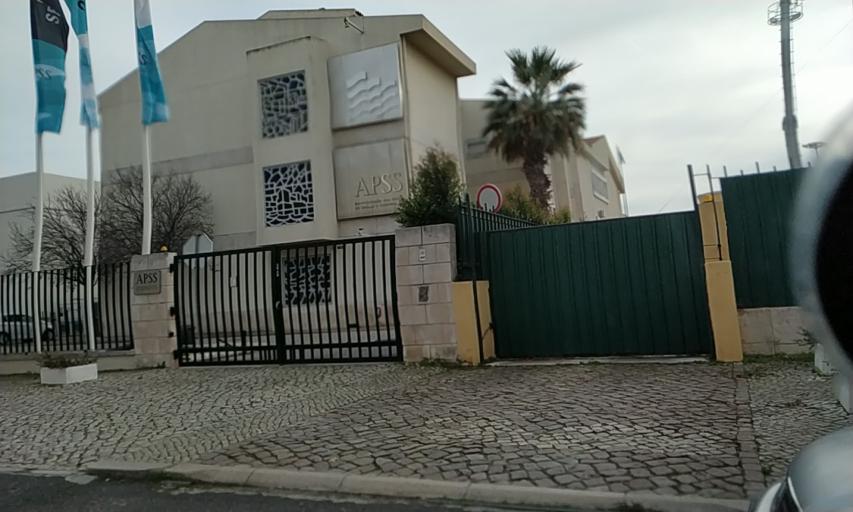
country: PT
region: Setubal
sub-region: Setubal
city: Setubal
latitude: 38.5224
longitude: -8.8909
